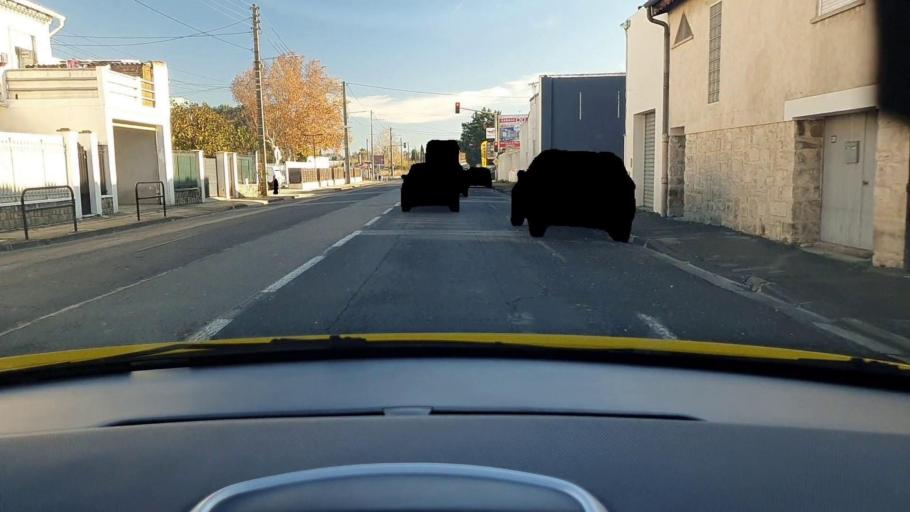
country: FR
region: Languedoc-Roussillon
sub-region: Departement du Gard
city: Nimes
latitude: 43.8256
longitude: 4.3778
